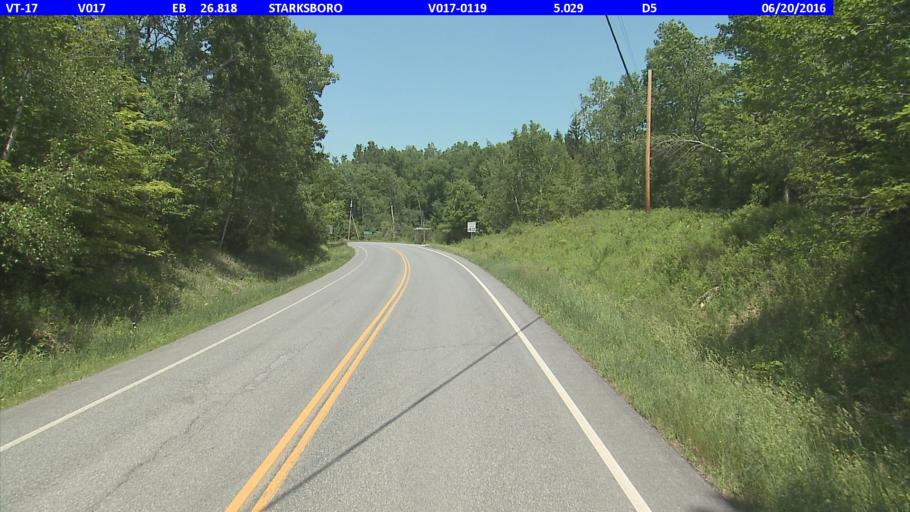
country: US
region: Vermont
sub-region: Addison County
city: Bristol
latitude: 44.2115
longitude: -72.9650
